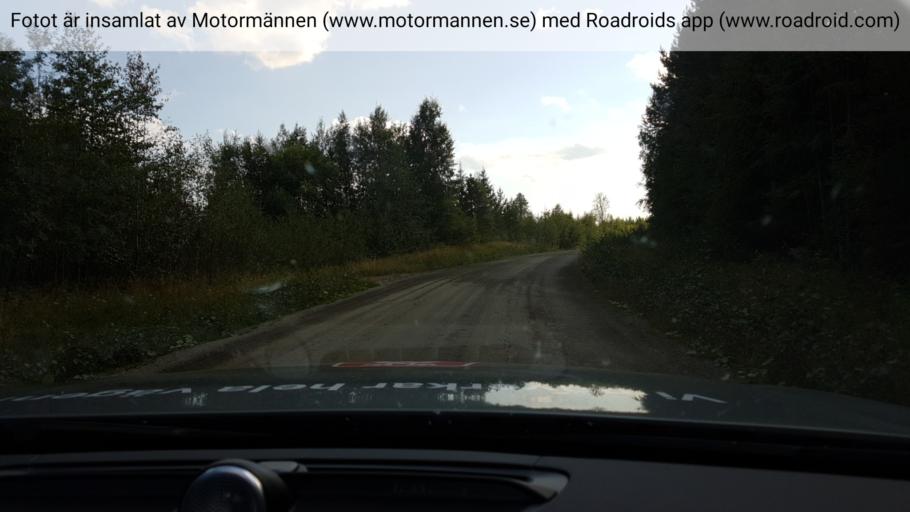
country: SE
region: Vaesternorrland
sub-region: Solleftea Kommun
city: As
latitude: 63.7948
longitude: 16.3961
